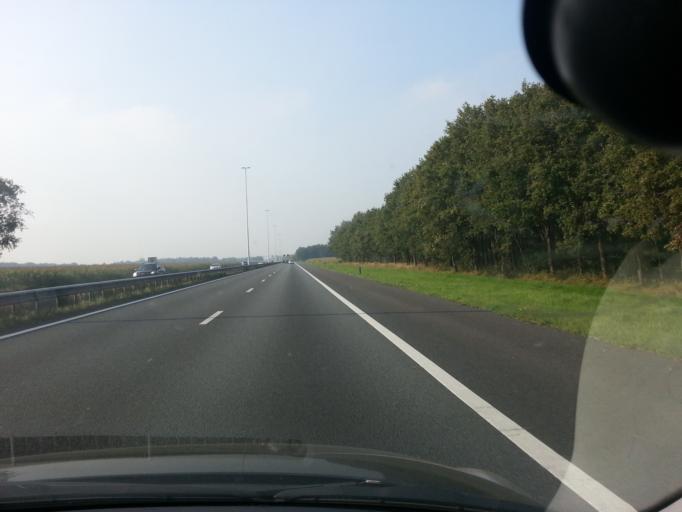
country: NL
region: North Brabant
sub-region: Gemeente Oirschot
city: Middelbeers
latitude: 51.5187
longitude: 5.2400
